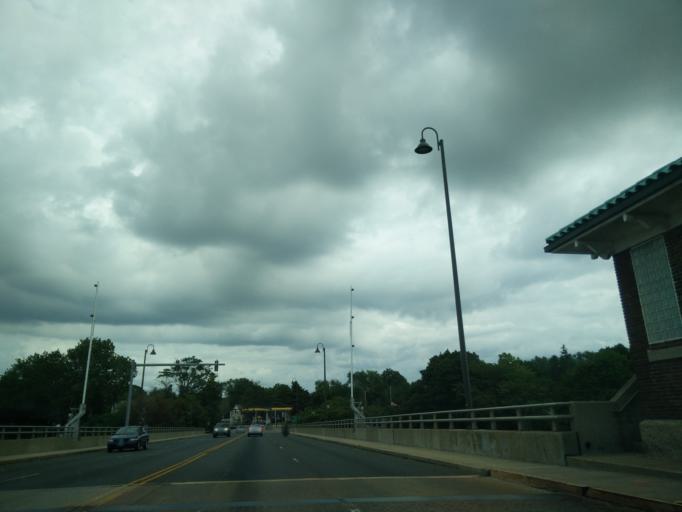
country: US
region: Connecticut
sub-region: Fairfield County
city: Stratford
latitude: 41.2002
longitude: -73.1104
